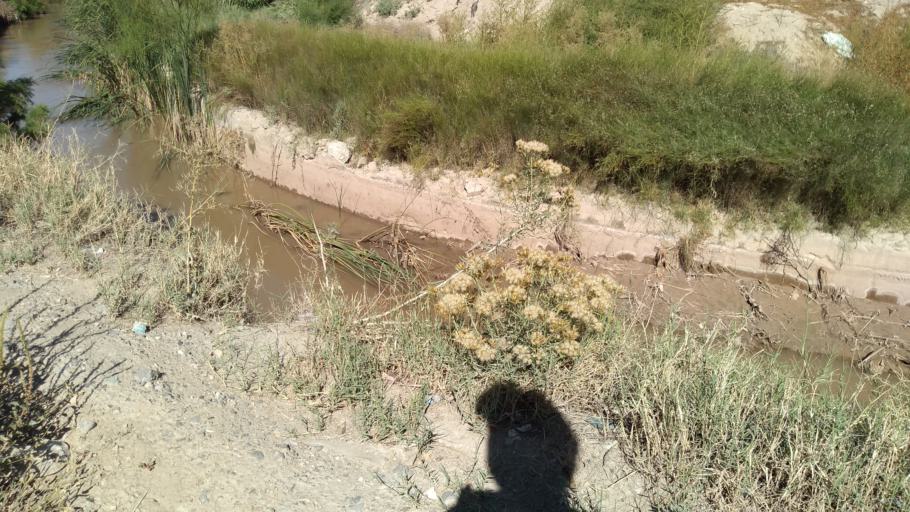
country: US
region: Texas
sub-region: El Paso County
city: El Paso
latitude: 31.7595
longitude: -106.5078
